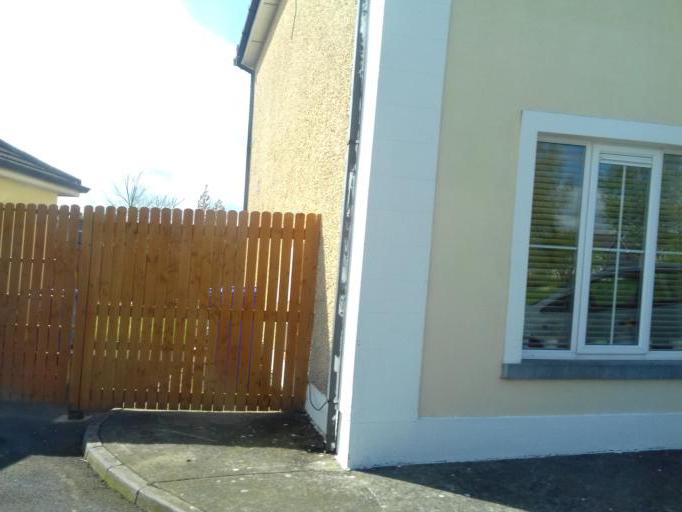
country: IE
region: Leinster
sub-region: Laois
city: Portlaoise
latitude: 53.0454
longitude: -7.2711
